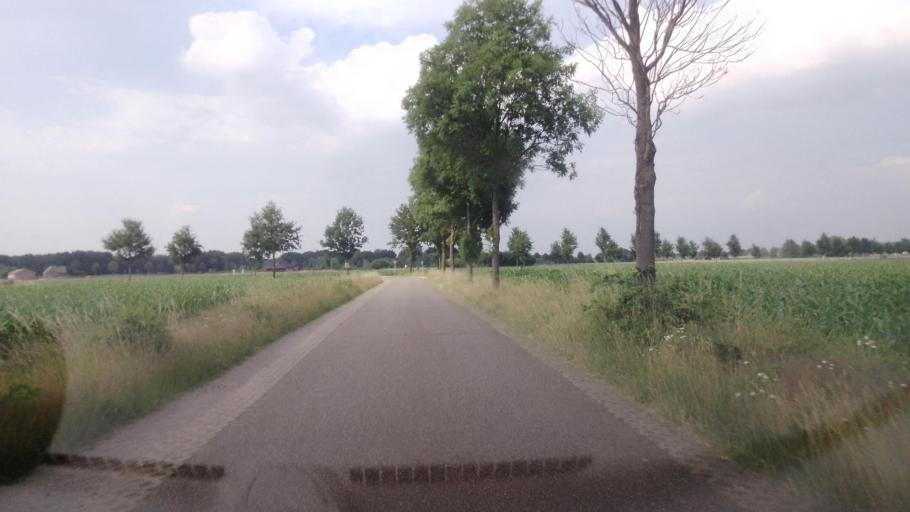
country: NL
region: Limburg
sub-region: Gemeente Peel en Maas
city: Maasbree
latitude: 51.3893
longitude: 6.0086
